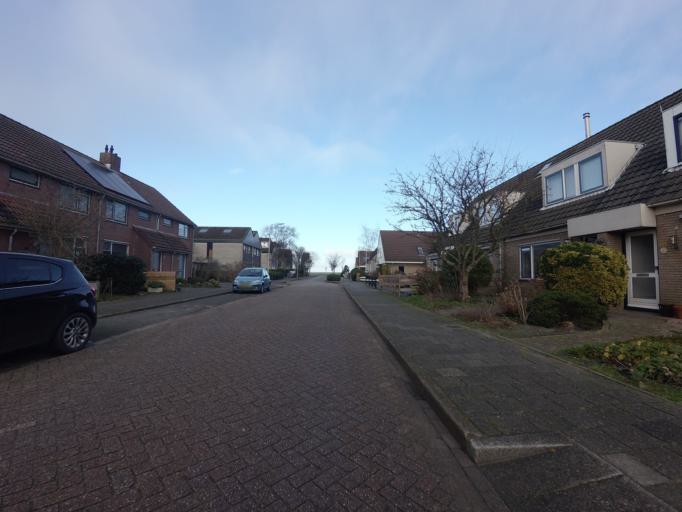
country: NL
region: North Holland
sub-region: Gemeente Texel
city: Den Burg
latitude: 53.1566
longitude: 4.8680
